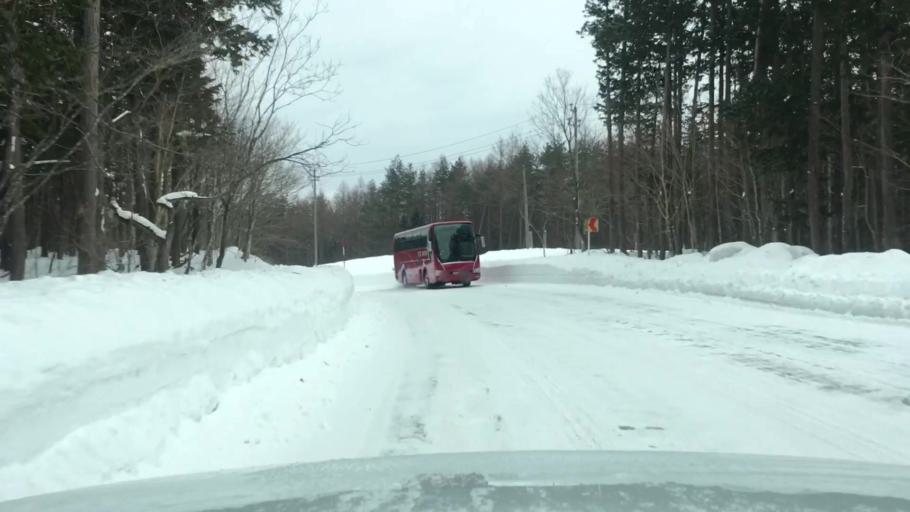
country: JP
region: Iwate
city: Shizukuishi
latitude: 39.9831
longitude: 141.0037
